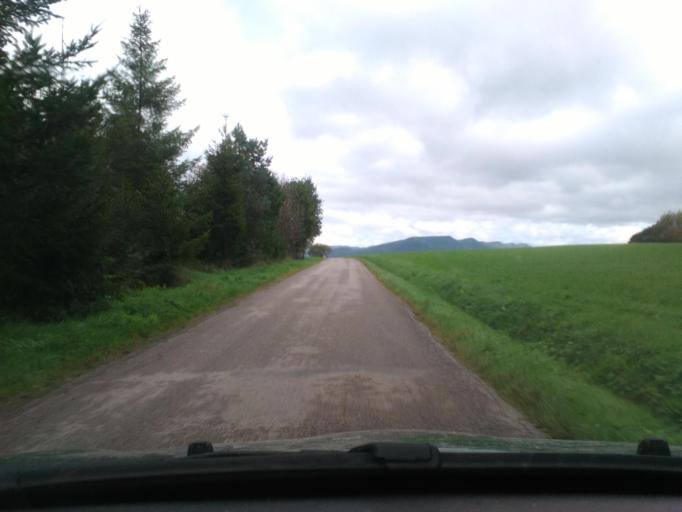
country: FR
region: Lorraine
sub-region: Departement des Vosges
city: Etival-Clairefontaine
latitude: 48.3456
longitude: 6.8582
